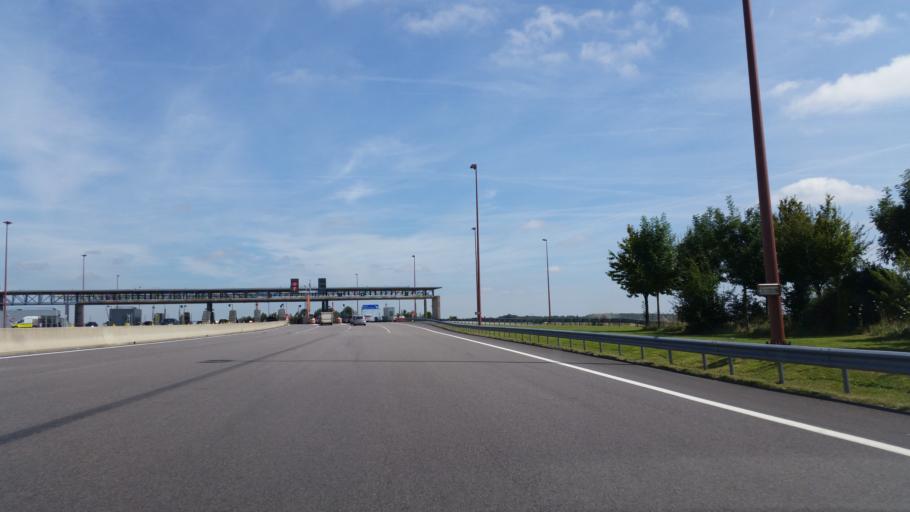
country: FR
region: Haute-Normandie
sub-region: Departement de la Seine-Maritime
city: Aumale
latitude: 49.7584
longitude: 1.7011
